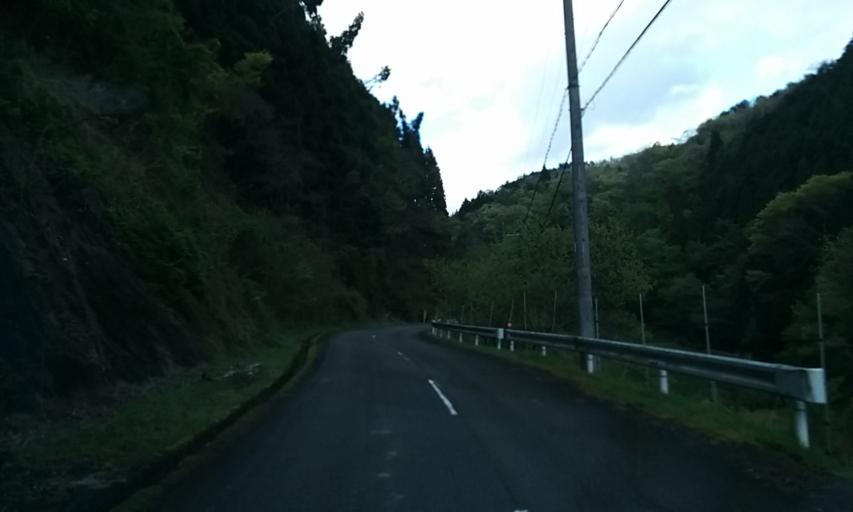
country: JP
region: Kyoto
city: Ayabe
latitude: 35.2515
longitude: 135.3083
